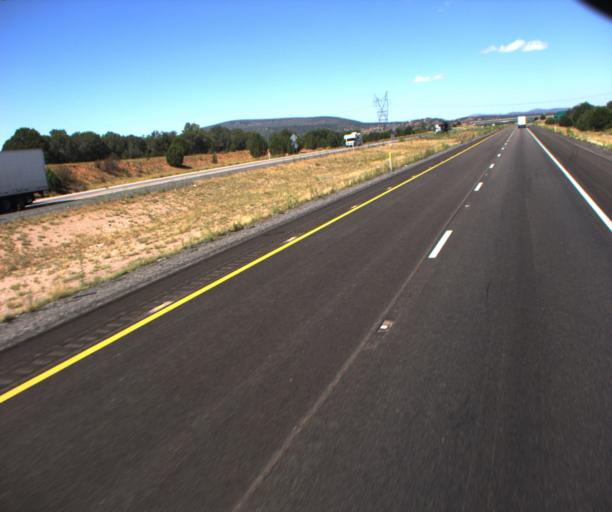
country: US
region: Arizona
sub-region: Mohave County
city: Peach Springs
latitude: 35.1911
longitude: -113.3566
